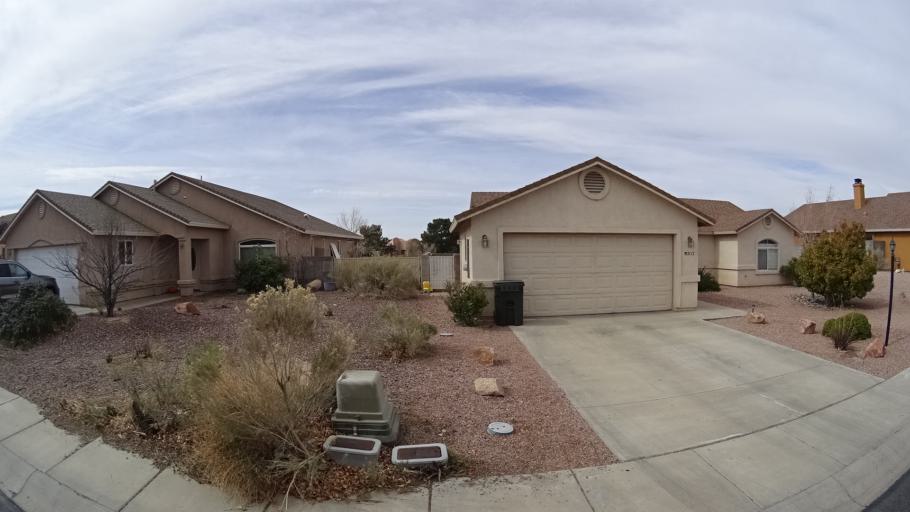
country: US
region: Arizona
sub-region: Mohave County
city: Kingman
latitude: 35.1854
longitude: -114.0098
